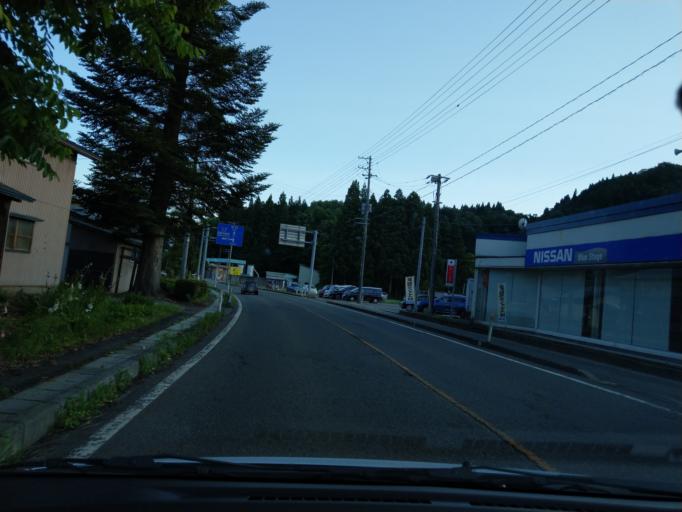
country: JP
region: Akita
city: Kakunodatemachi
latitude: 39.6083
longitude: 140.5682
